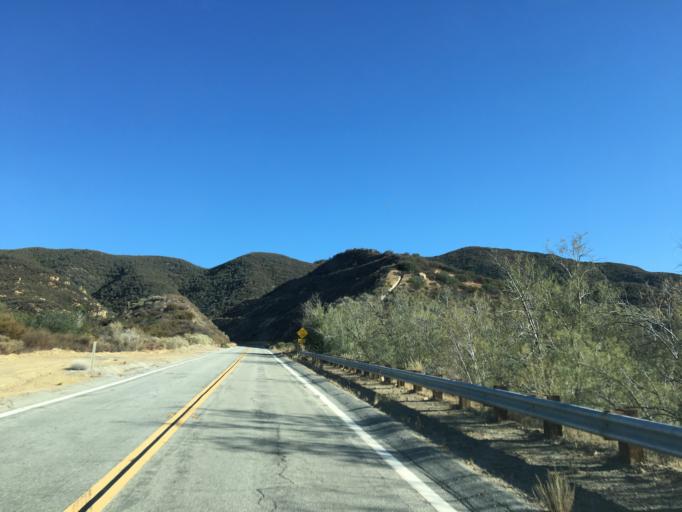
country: US
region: California
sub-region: Los Angeles County
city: Castaic
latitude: 34.5585
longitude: -118.5423
